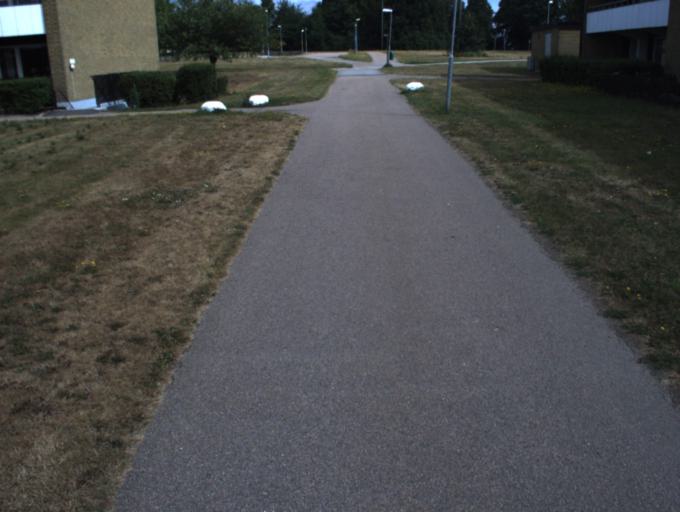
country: SE
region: Skane
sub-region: Helsingborg
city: Barslov
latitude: 56.0079
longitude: 12.8102
